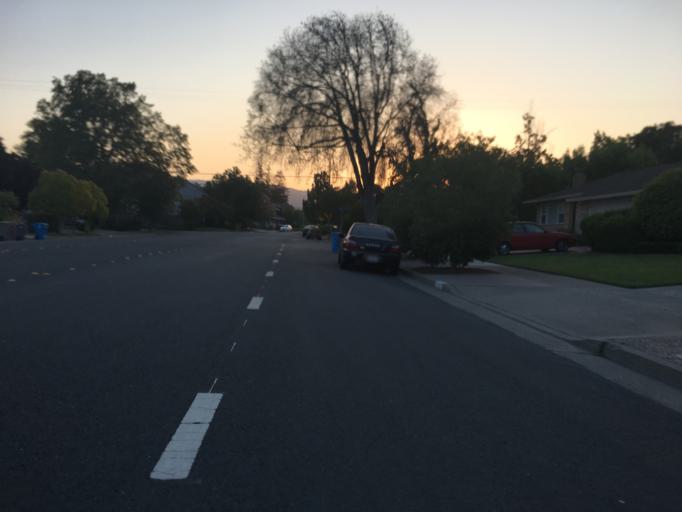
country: US
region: California
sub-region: Santa Clara County
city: Cupertino
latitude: 37.3124
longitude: -122.0365
